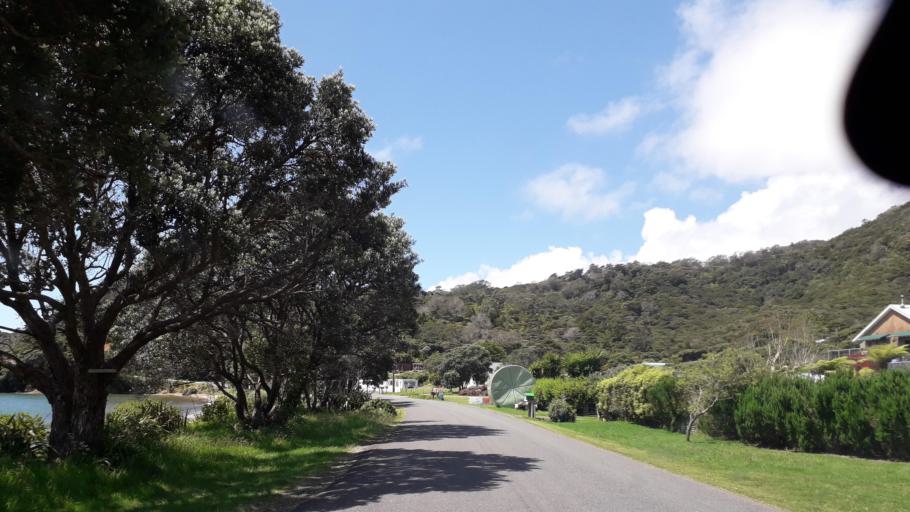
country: NZ
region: Northland
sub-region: Far North District
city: Paihia
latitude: -35.2371
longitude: 174.2592
